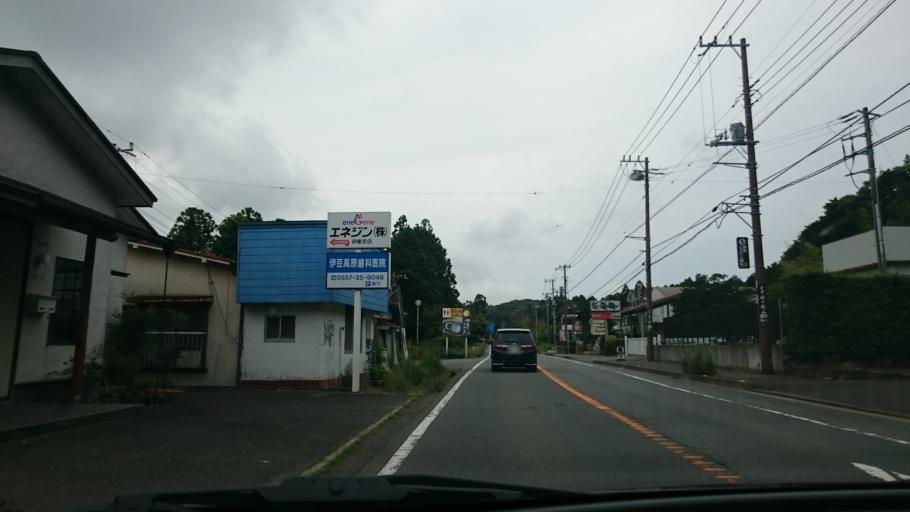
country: JP
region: Shizuoka
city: Ito
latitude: 34.9181
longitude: 139.1203
